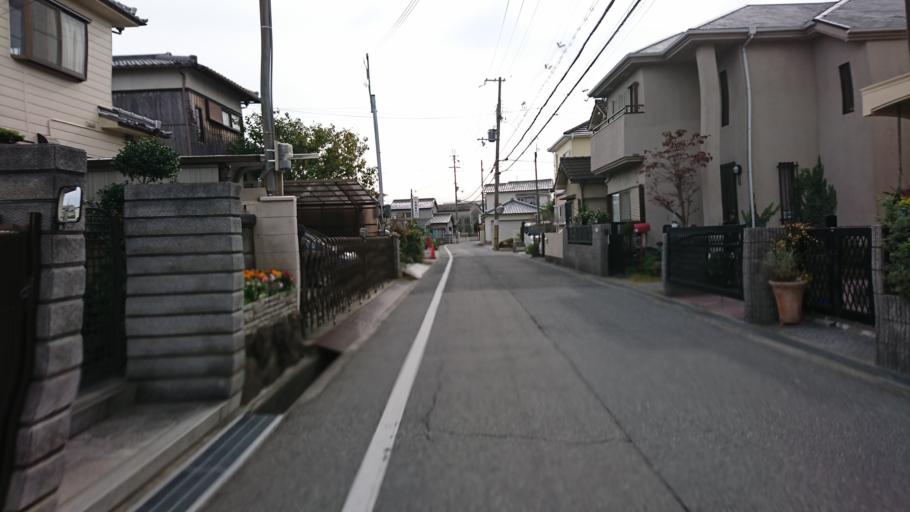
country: JP
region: Hyogo
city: Kakogawacho-honmachi
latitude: 34.7742
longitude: 134.8559
